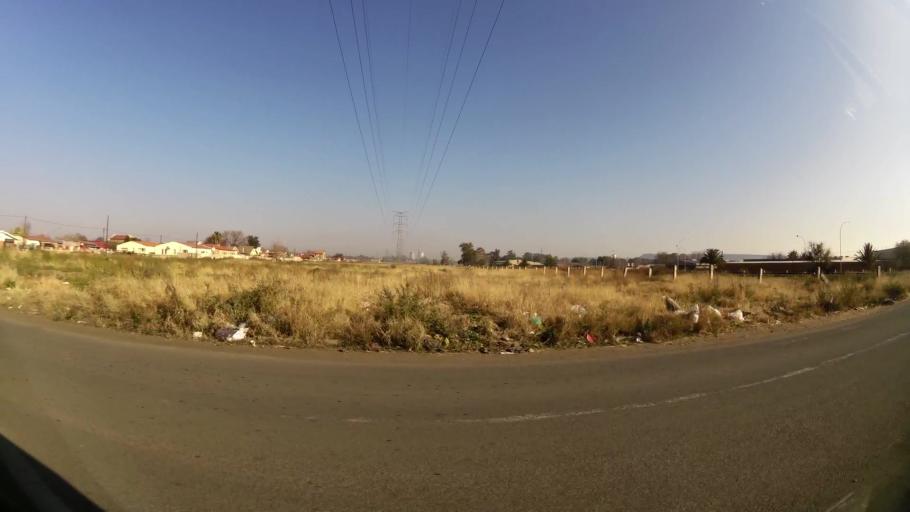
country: ZA
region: Orange Free State
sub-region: Mangaung Metropolitan Municipality
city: Bloemfontein
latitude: -29.1318
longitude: 26.2535
